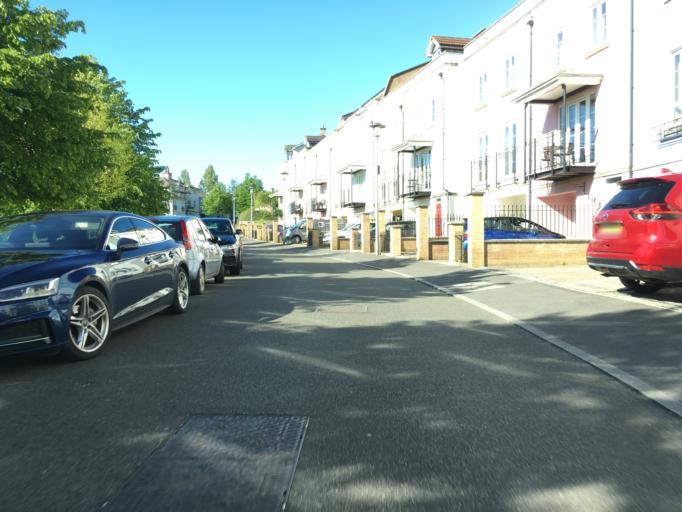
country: GB
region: England
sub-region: North Somerset
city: Portishead
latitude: 51.4915
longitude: -2.7624
